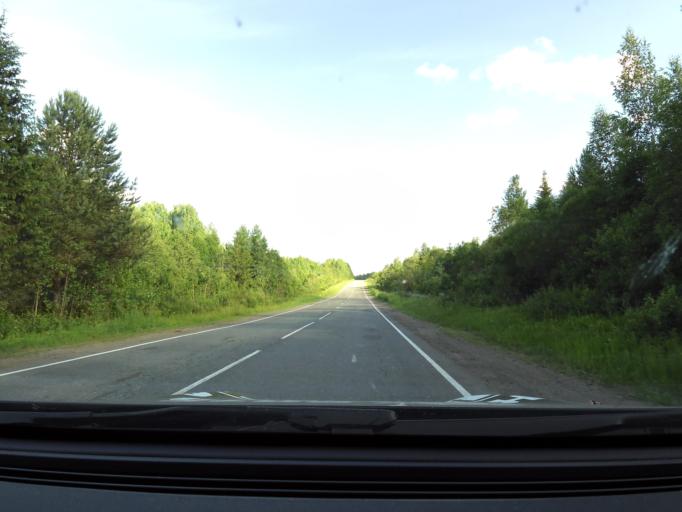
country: RU
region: Kirov
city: Omutninsk
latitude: 58.7146
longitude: 52.0933
